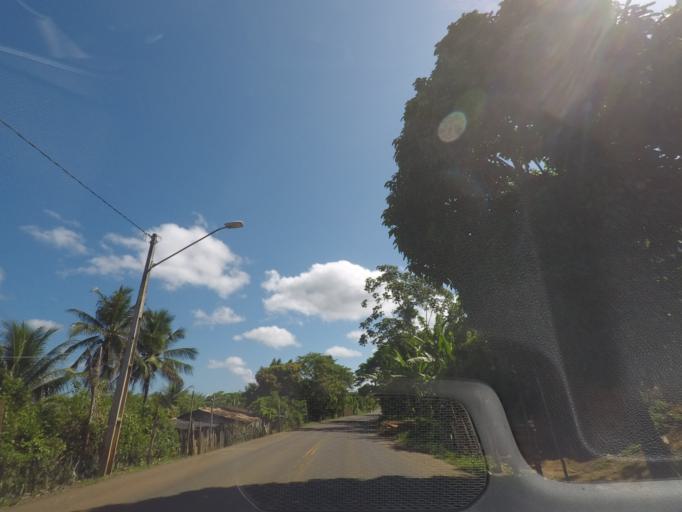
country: BR
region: Bahia
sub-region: Itubera
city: Itubera
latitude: -13.7586
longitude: -39.1518
